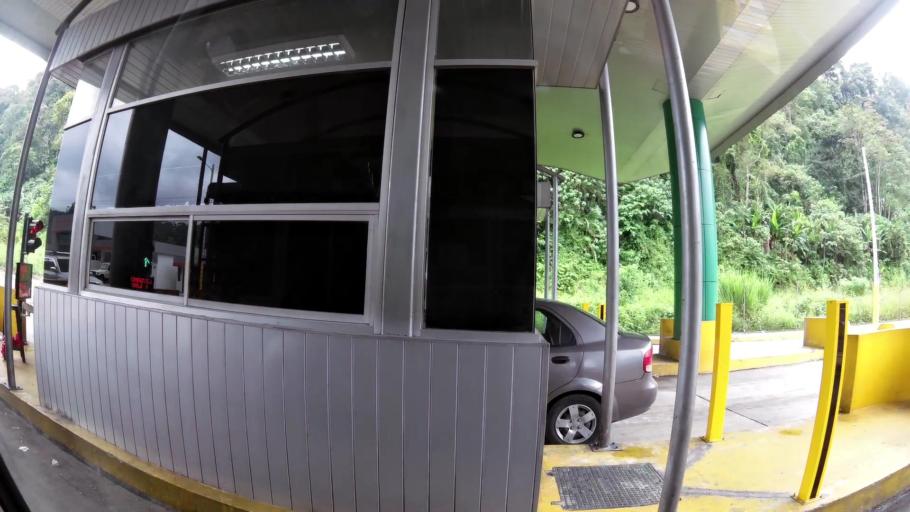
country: EC
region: Santo Domingo de los Tsachilas
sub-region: Canton Santo Domingo de los Colorados
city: Santo Domingo de los Colorados
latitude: -0.2755
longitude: -79.0780
